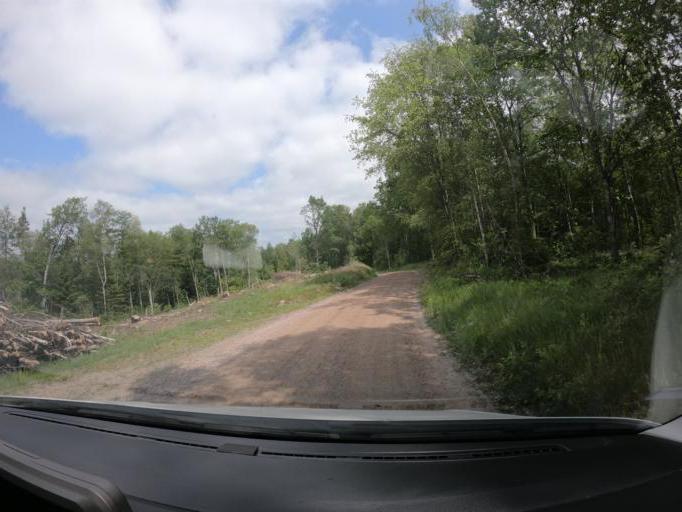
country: SE
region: Skane
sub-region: Hoors Kommun
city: Hoeoer
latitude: 56.0383
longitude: 13.5417
